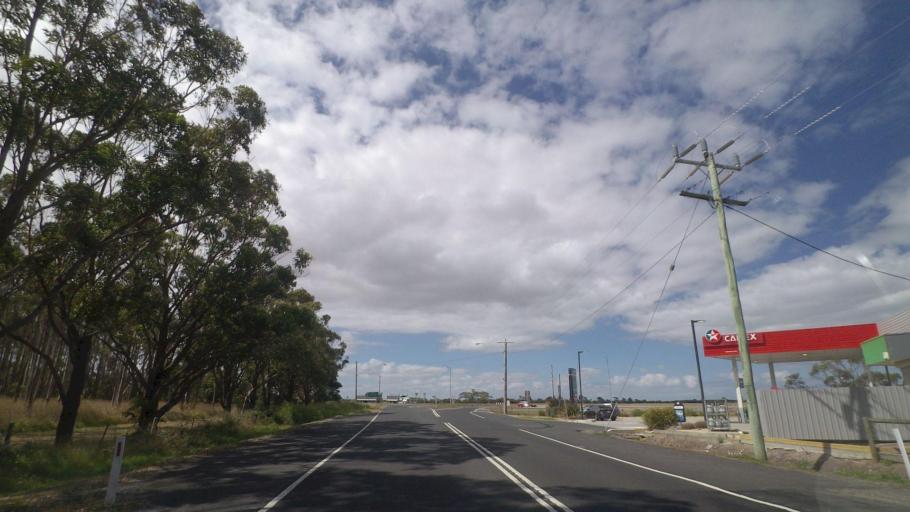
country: AU
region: Victoria
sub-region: Cardinia
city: Koo-Wee-Rup
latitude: -38.2144
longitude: 145.4972
